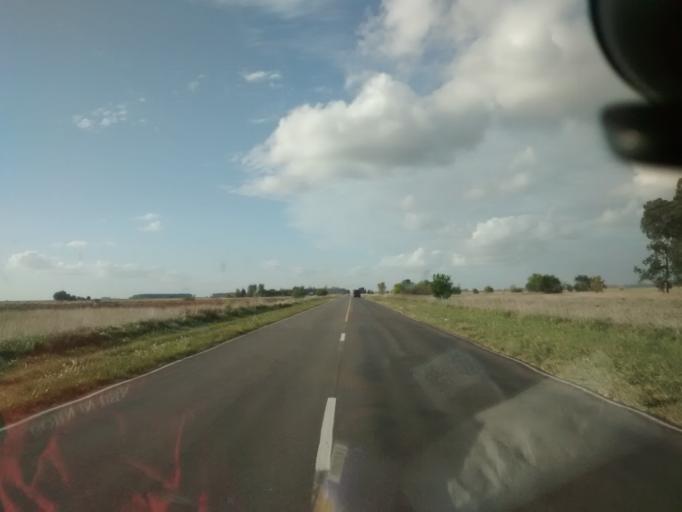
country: AR
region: Buenos Aires
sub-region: Partido de Ayacucho
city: Ayacucho
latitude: -36.6466
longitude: -58.5735
